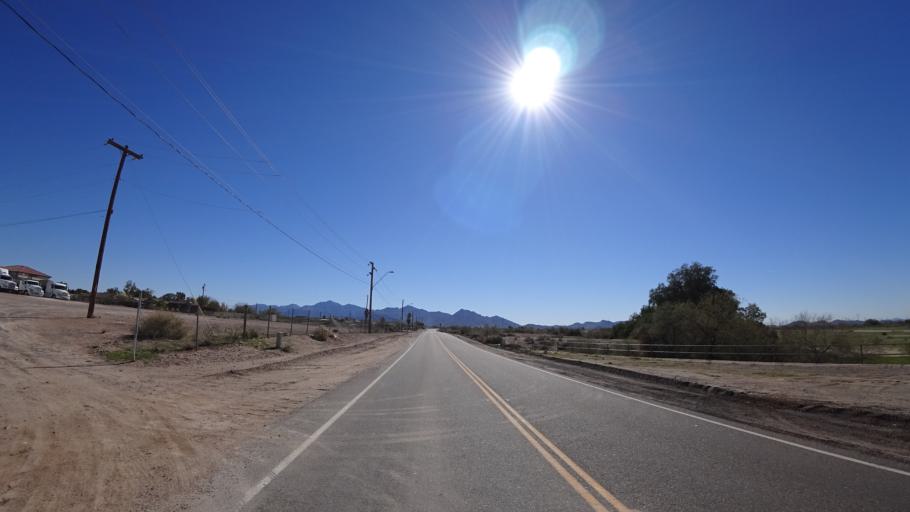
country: US
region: Arizona
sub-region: Maricopa County
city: Avondale
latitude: 33.4197
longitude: -112.3323
